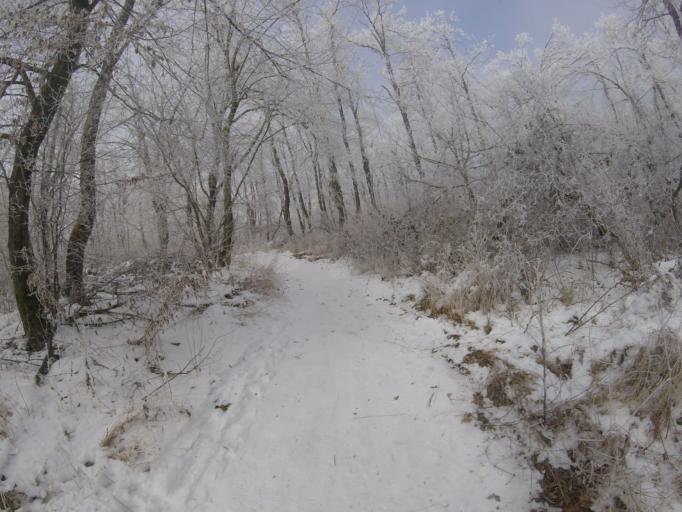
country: HU
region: Pest
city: Pilisszentivan
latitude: 47.5898
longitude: 18.9026
